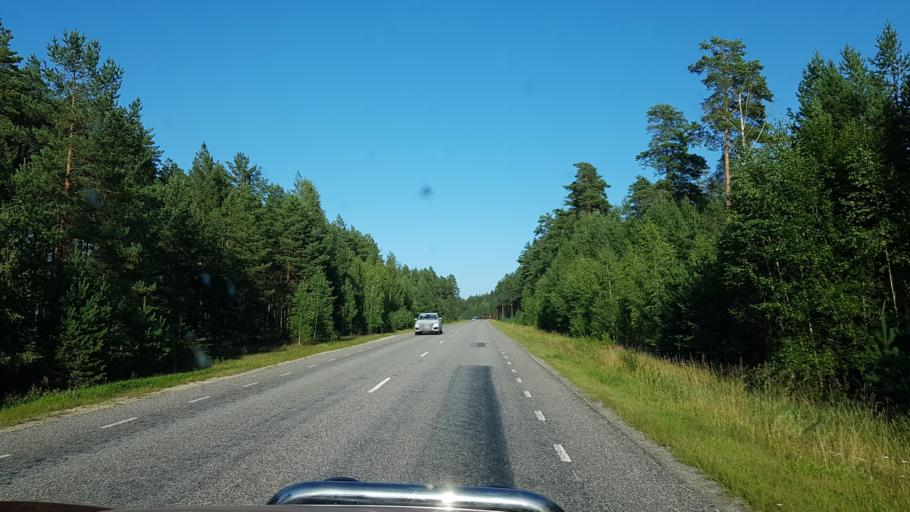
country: RU
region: Pskov
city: Pechory
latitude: 57.8146
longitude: 27.3247
